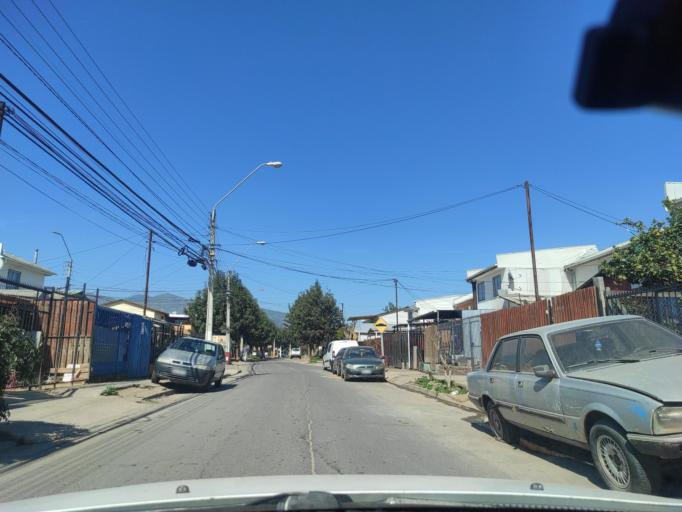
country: CL
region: Valparaiso
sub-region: Provincia de Marga Marga
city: Limache
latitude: -33.0179
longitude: -71.2636
